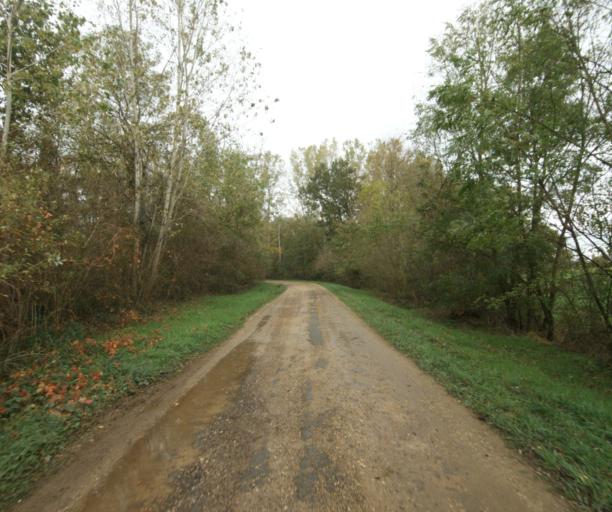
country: FR
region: Rhone-Alpes
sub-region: Departement de l'Ain
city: Pont-de-Vaux
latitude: 46.4623
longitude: 4.9060
